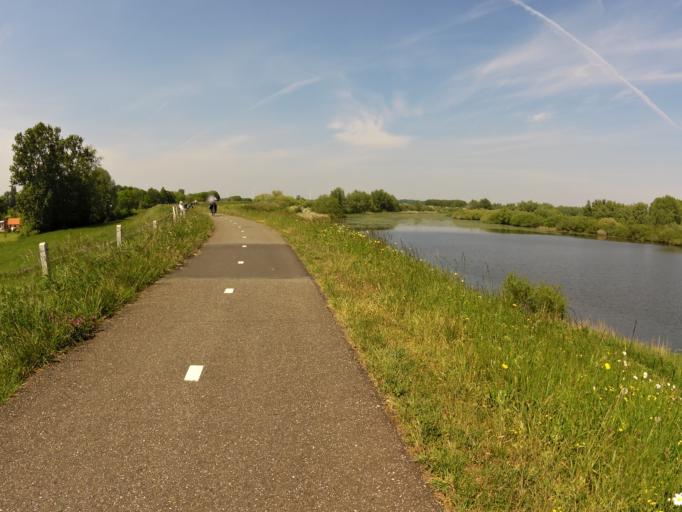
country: NL
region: Gelderland
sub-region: Gemeente Neerijnen
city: Neerijnen
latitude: 51.8067
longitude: 5.2841
